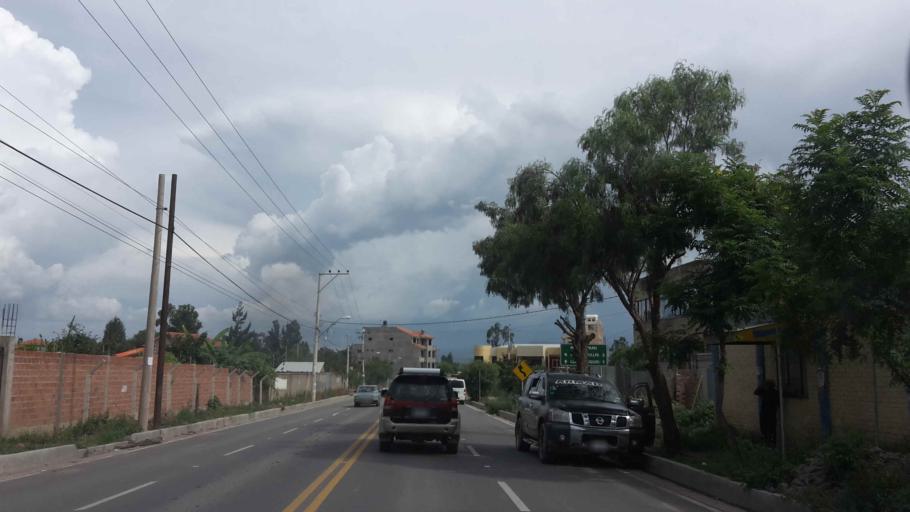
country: BO
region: Cochabamba
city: Cochabamba
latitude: -17.3521
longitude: -66.2557
